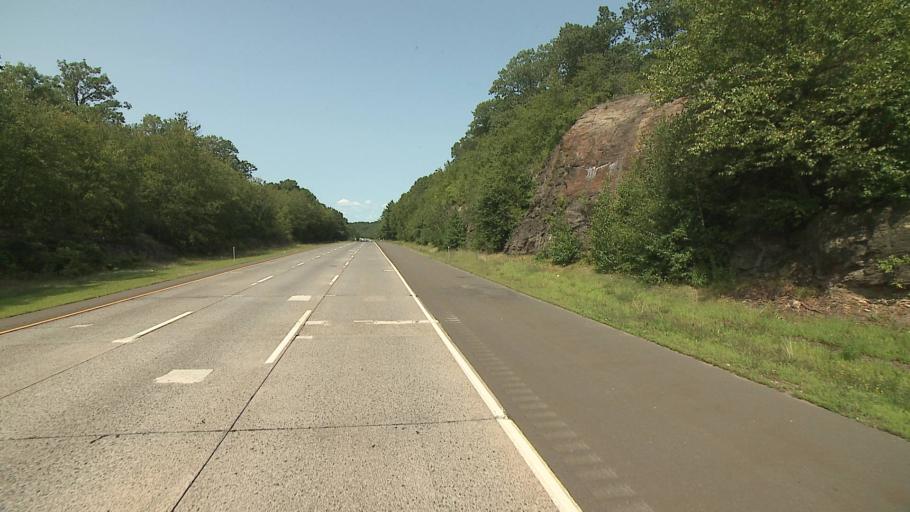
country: US
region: Connecticut
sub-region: Fairfield County
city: Trumbull
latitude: 41.2661
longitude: -73.2099
